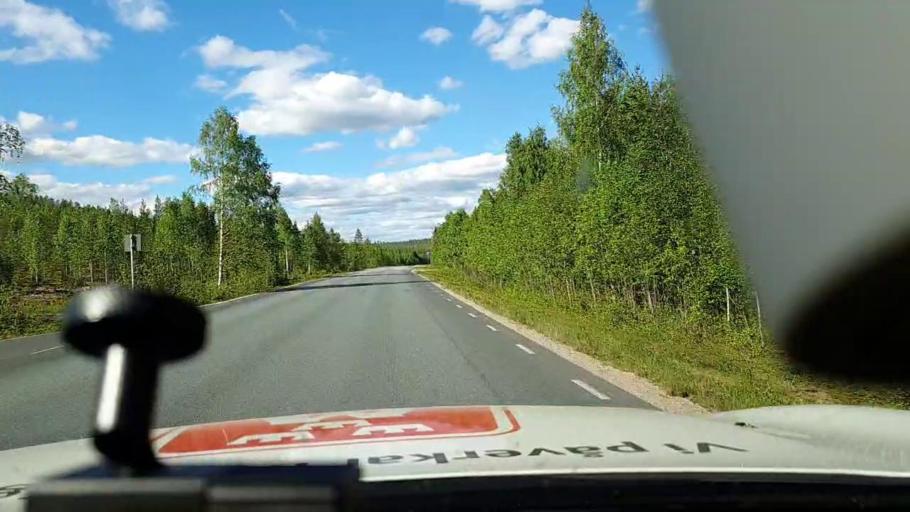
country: FI
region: Lapland
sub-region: Torniolaakso
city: Ylitornio
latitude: 66.3157
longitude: 23.6195
